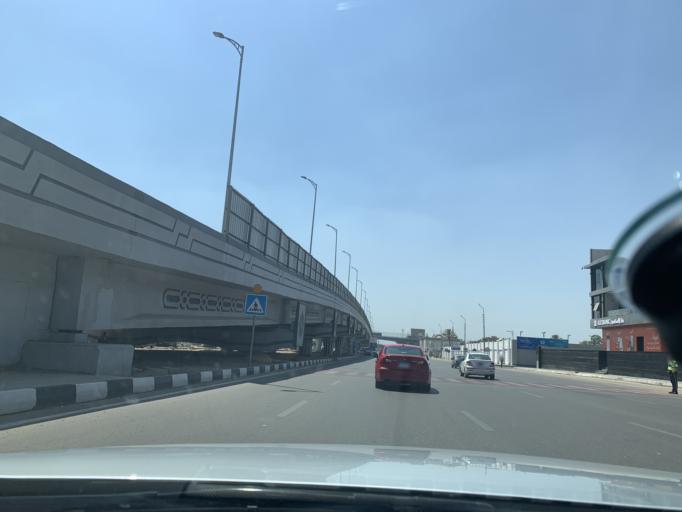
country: EG
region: Muhafazat al Qahirah
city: Cairo
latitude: 30.0923
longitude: 31.3476
